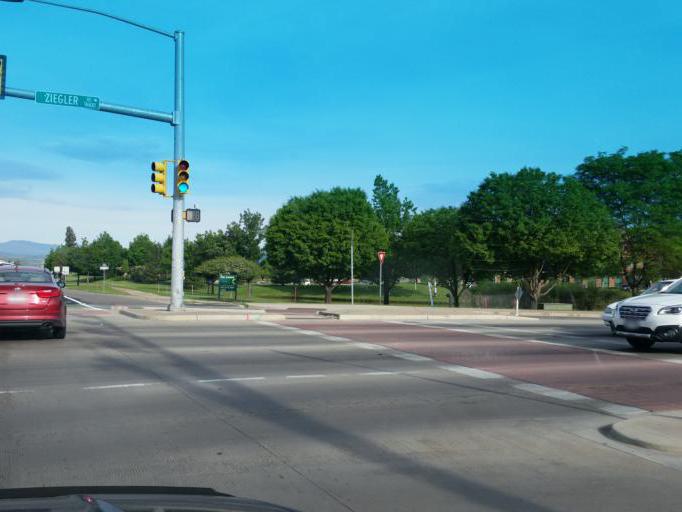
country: US
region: Colorado
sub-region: Larimer County
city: Fort Collins
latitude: 40.5234
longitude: -105.0201
